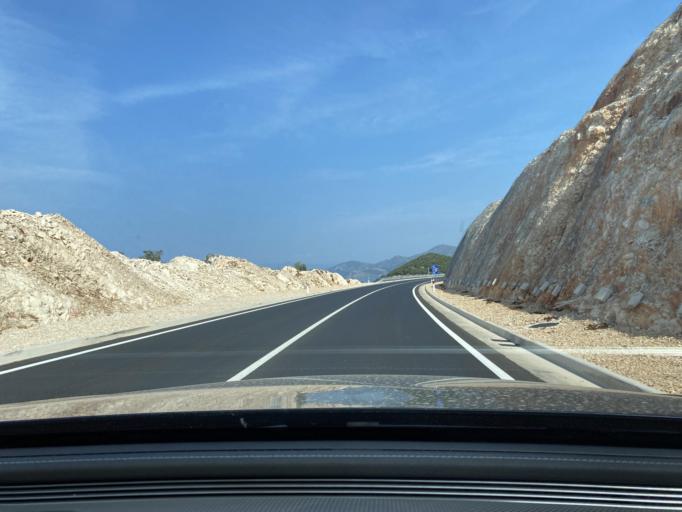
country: BA
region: Federation of Bosnia and Herzegovina
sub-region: Hercegovacko-Bosanski Kanton
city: Neum
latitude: 42.9121
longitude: 17.5286
